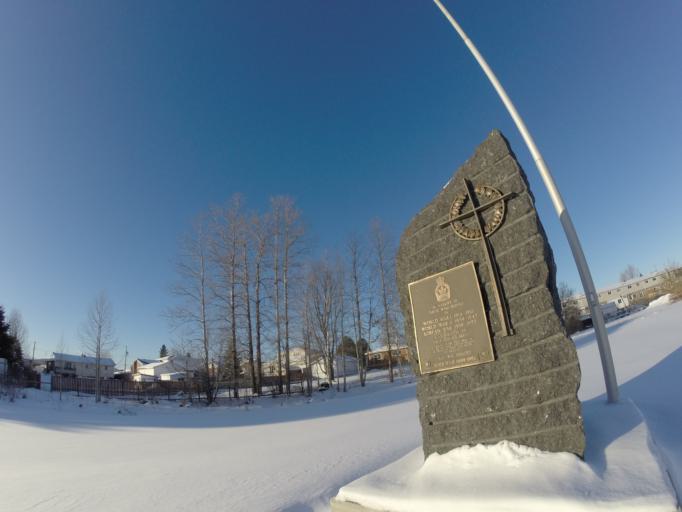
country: CA
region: Ontario
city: Rayside-Balfour
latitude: 46.5761
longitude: -81.1941
